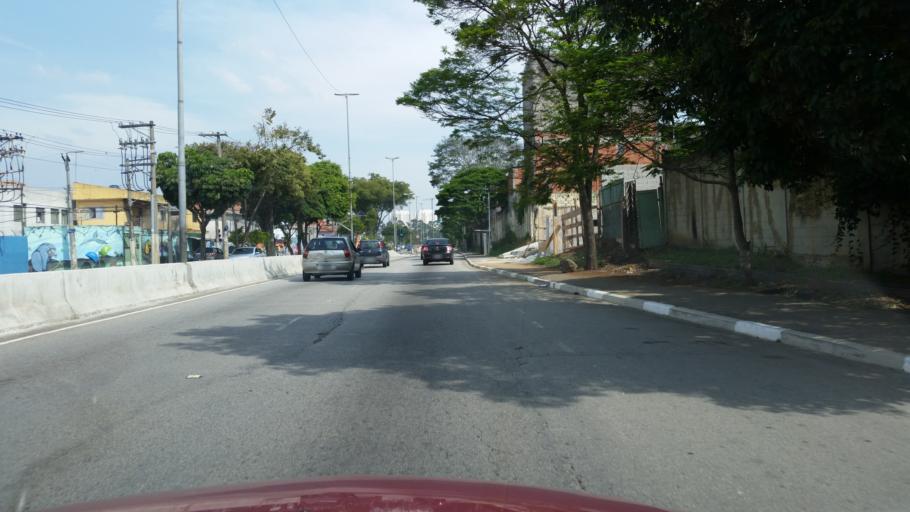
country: BR
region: Sao Paulo
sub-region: Ferraz De Vasconcelos
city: Ferraz de Vasconcelos
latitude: -23.5281
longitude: -46.4316
